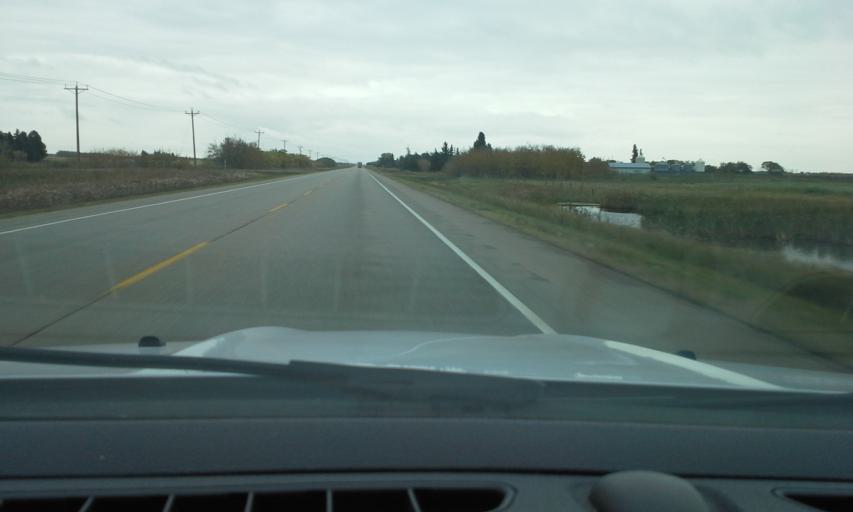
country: CA
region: Saskatchewan
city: Lloydminster
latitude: 53.2780
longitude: -109.8603
